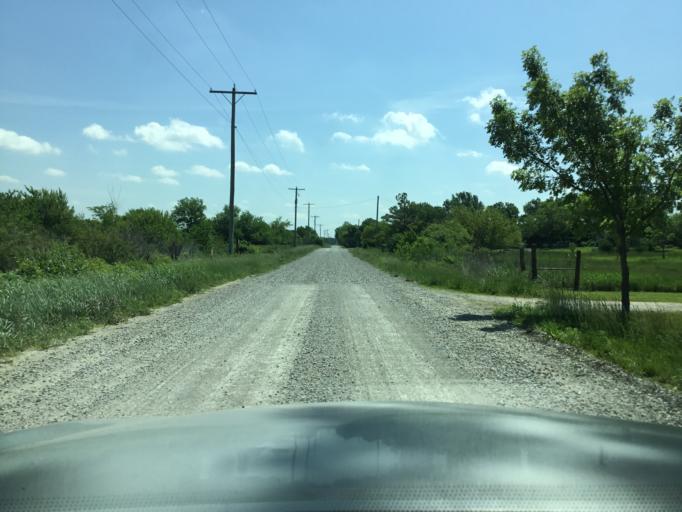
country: US
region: Kansas
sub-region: Labette County
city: Parsons
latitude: 37.3110
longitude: -95.2607
